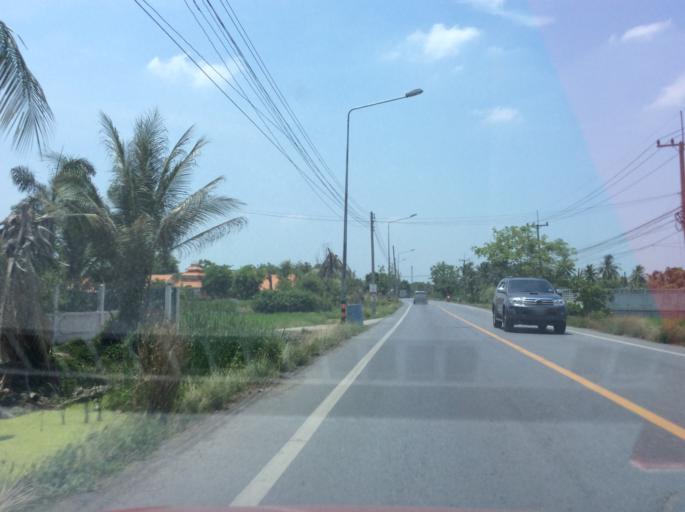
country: TH
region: Pathum Thani
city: Ban Lam Luk Ka
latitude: 13.9912
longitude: 100.7778
